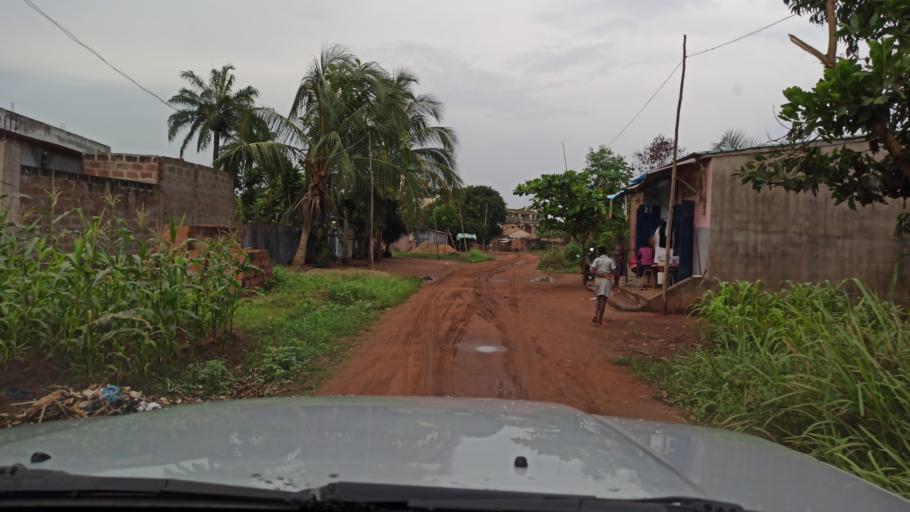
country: BJ
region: Queme
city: Porto-Novo
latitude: 6.4746
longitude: 2.6741
